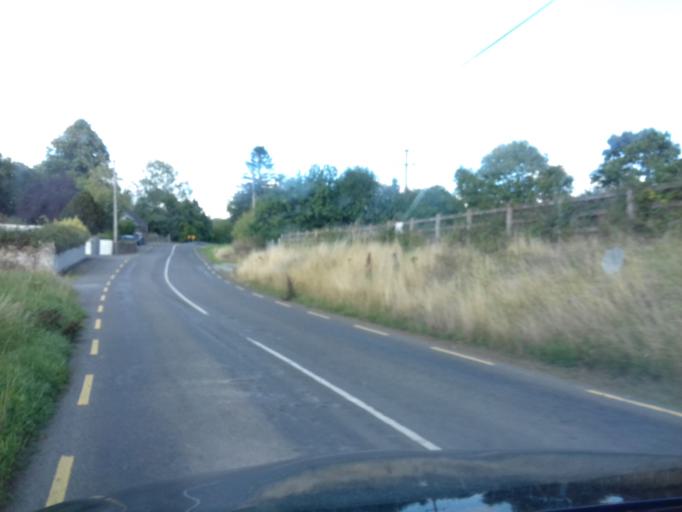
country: IE
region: Leinster
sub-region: Kilkenny
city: Thomastown
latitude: 52.5358
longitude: -7.1061
